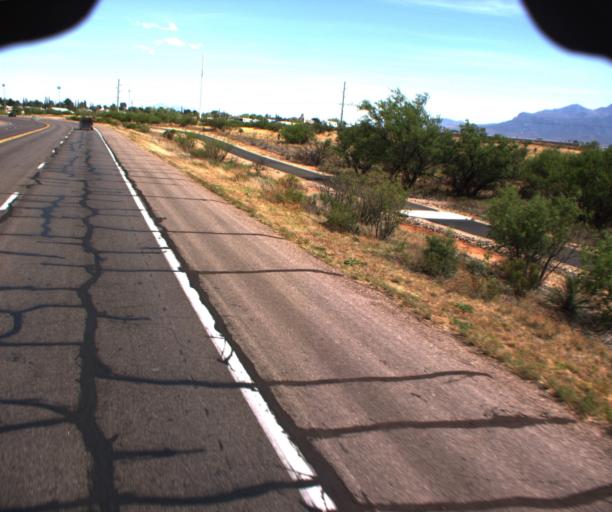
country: US
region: Arizona
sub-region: Cochise County
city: Sierra Vista
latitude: 31.5711
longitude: -110.3083
